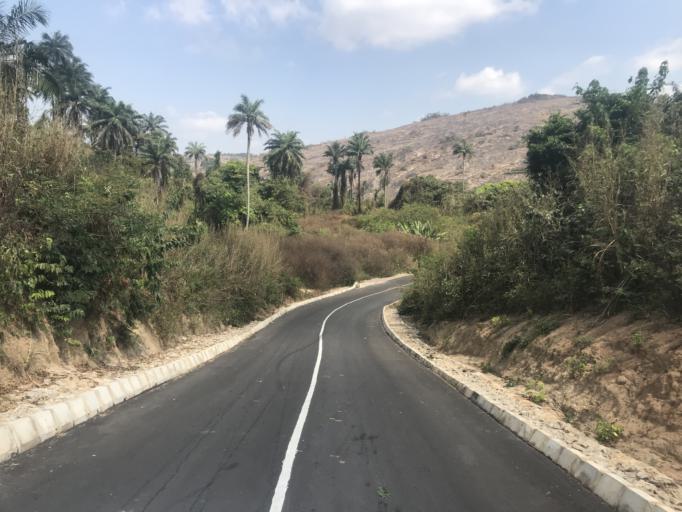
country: NG
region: Osun
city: Otan Ayegbaju
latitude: 7.9060
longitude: 4.8272
